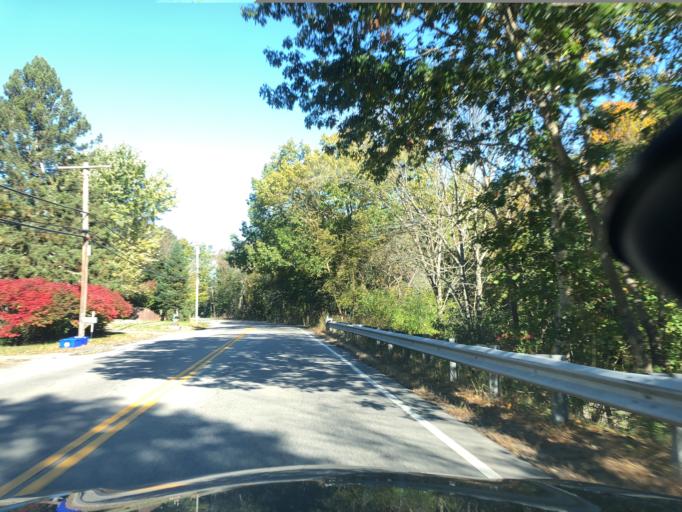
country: US
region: New Hampshire
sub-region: Rockingham County
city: Newmarket
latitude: 43.0648
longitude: -70.9364
